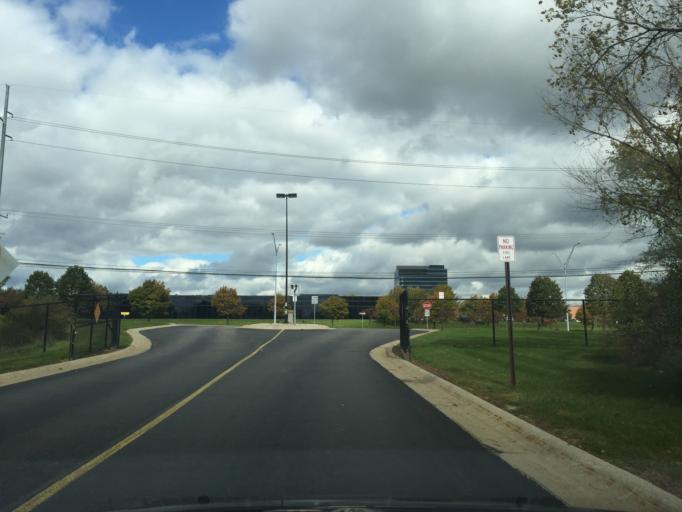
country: US
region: Michigan
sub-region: Oakland County
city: Auburn Hills
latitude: 42.6486
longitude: -83.2349
